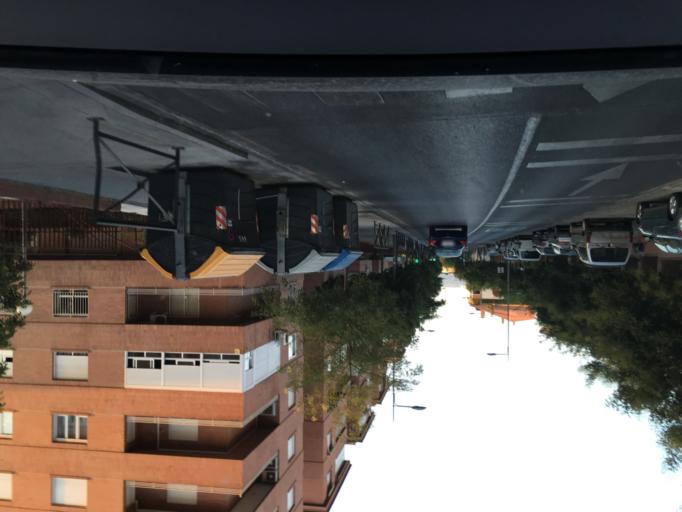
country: ES
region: Andalusia
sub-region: Provincia de Granada
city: Granada
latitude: 37.1915
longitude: -3.6039
